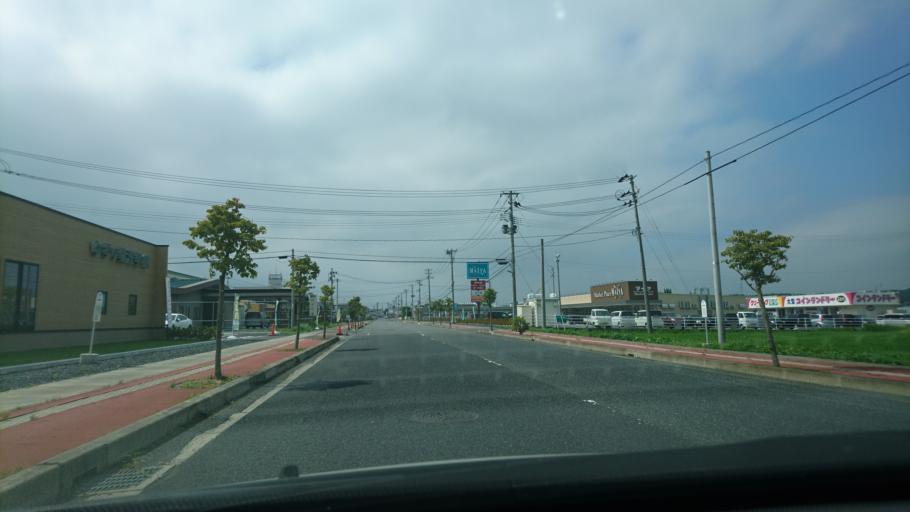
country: JP
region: Iwate
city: Ichinoseki
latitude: 38.8288
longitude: 141.1867
